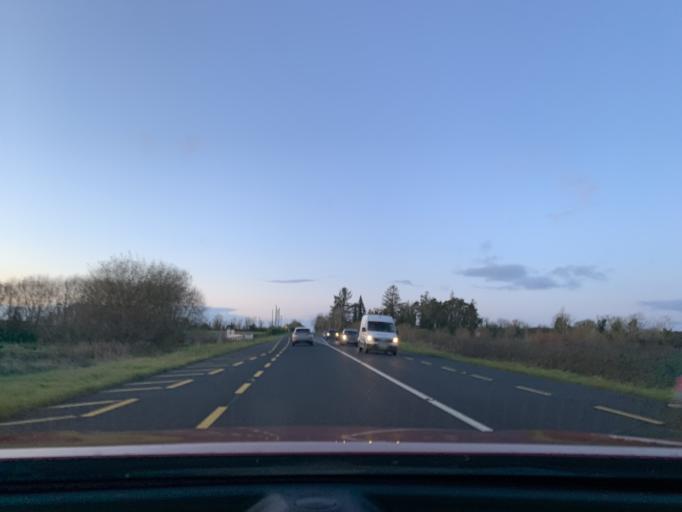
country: IE
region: Connaught
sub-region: County Leitrim
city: Carrick-on-Shannon
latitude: 53.8934
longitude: -7.9487
